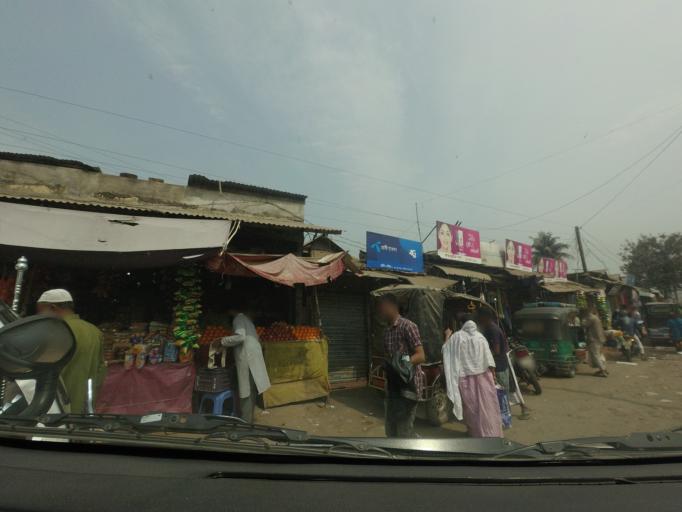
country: BD
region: Dhaka
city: Kishorganj
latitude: 24.3472
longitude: 90.7552
